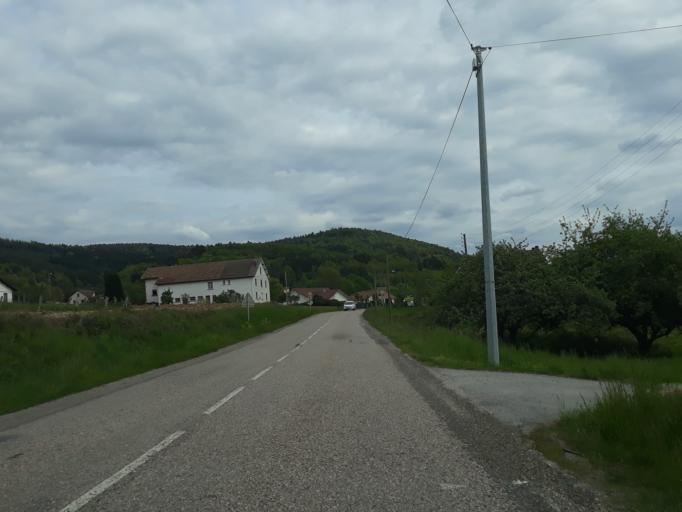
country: FR
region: Lorraine
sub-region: Departement des Vosges
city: Granges-sur-Vologne
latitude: 48.1715
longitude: 6.7732
